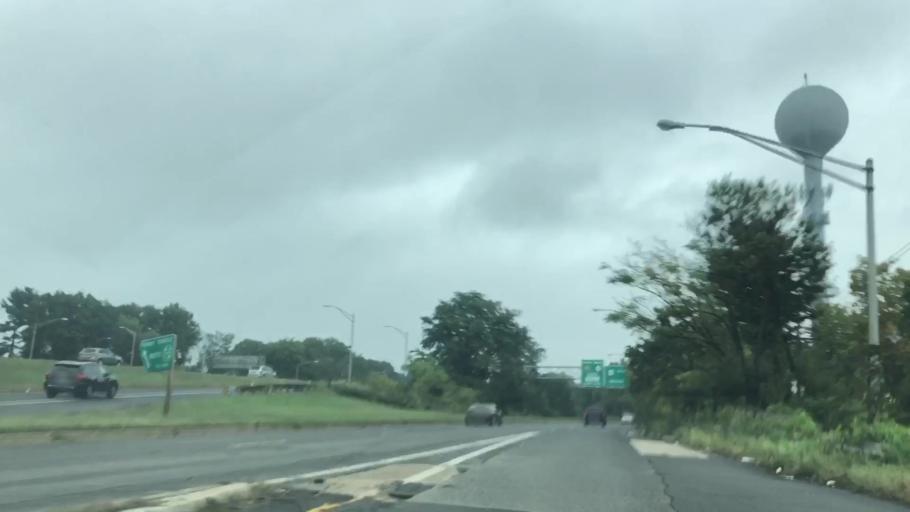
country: US
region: New Jersey
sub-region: Union County
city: Union
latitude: 40.6925
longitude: -74.2636
